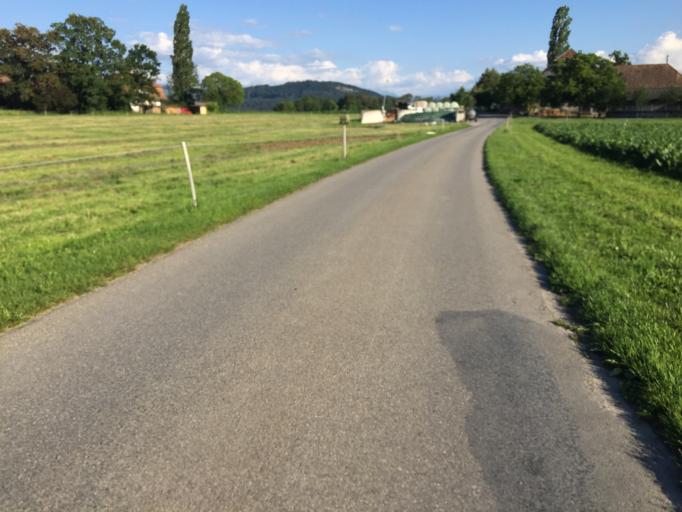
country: CH
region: Bern
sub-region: Bern-Mittelland District
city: Niederwichtrach
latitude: 46.8279
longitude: 7.5886
